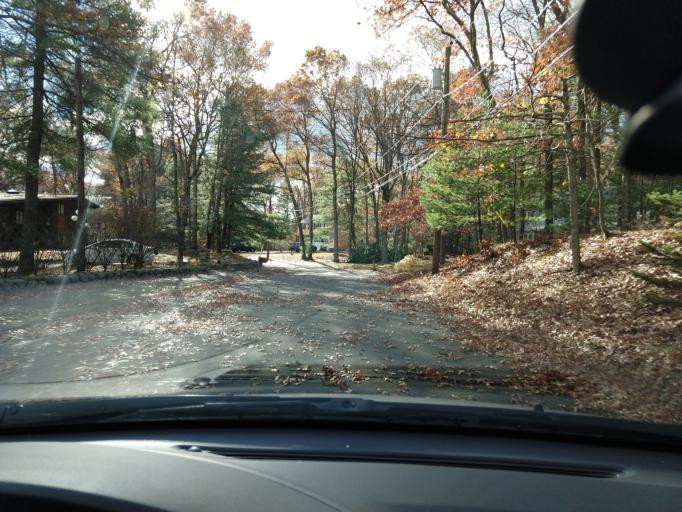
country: US
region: Massachusetts
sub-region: Middlesex County
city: Bedford
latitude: 42.4907
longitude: -71.2441
